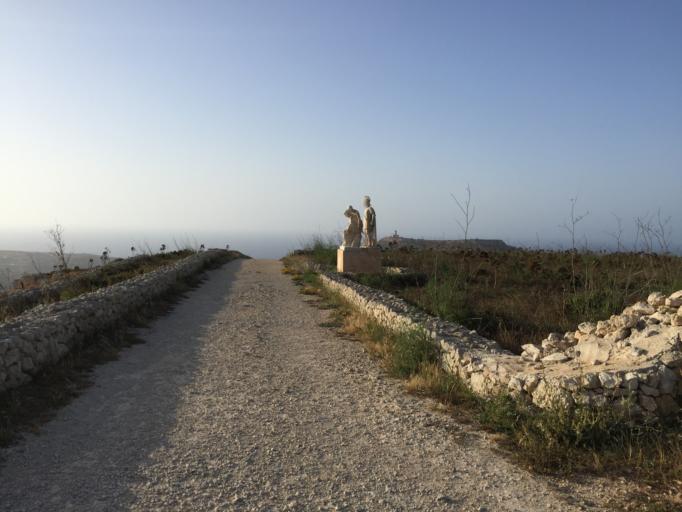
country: MT
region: L-Gharb
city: Gharb
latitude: 36.0588
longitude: 14.2191
